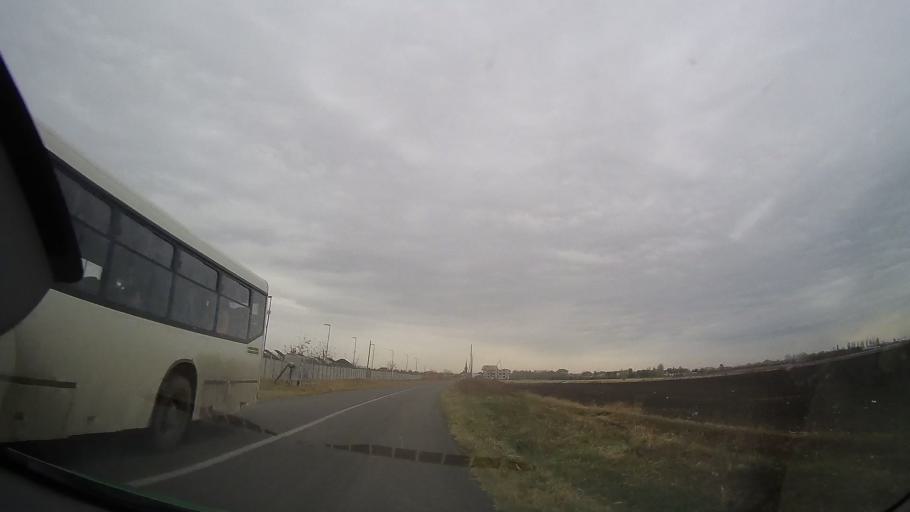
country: RO
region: Prahova
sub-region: Oras Mizil
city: Mizil
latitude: 45.0063
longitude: 26.4250
